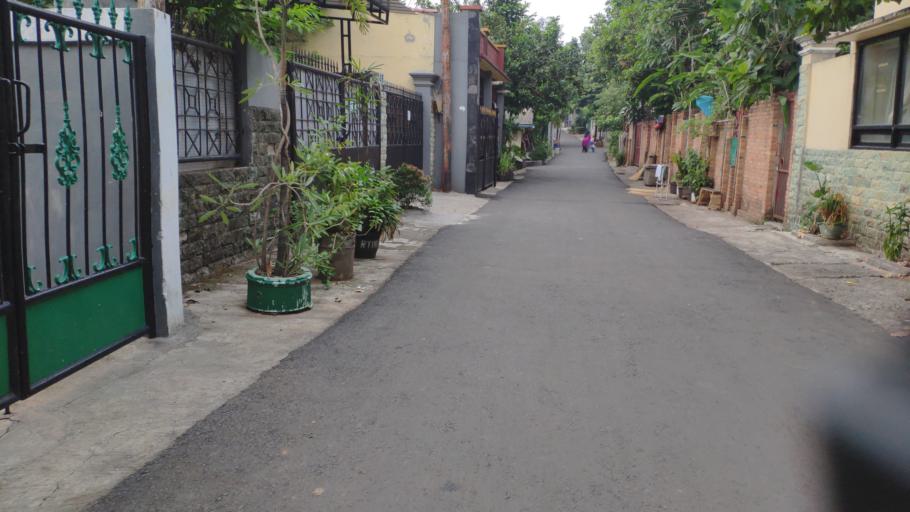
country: ID
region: West Java
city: Depok
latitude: -6.3197
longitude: 106.8214
